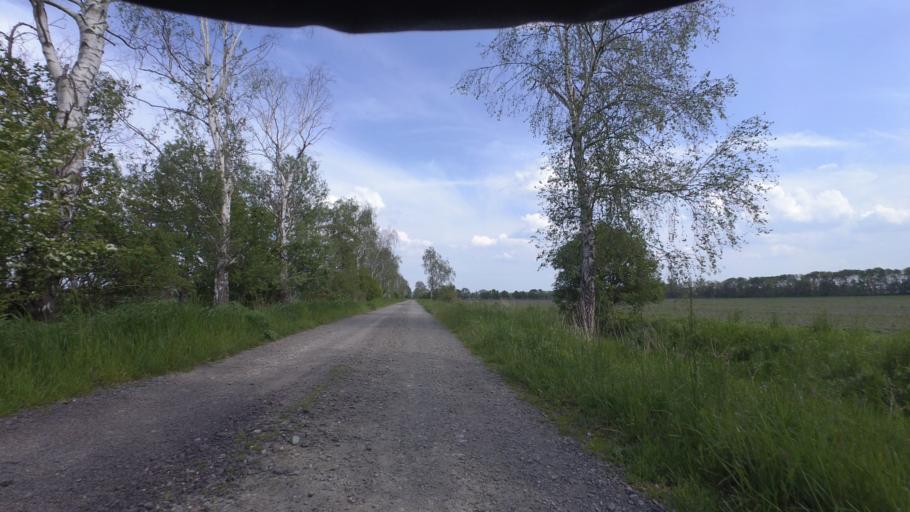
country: DE
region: Lower Saxony
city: Sollingen
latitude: 52.0660
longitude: 10.9322
